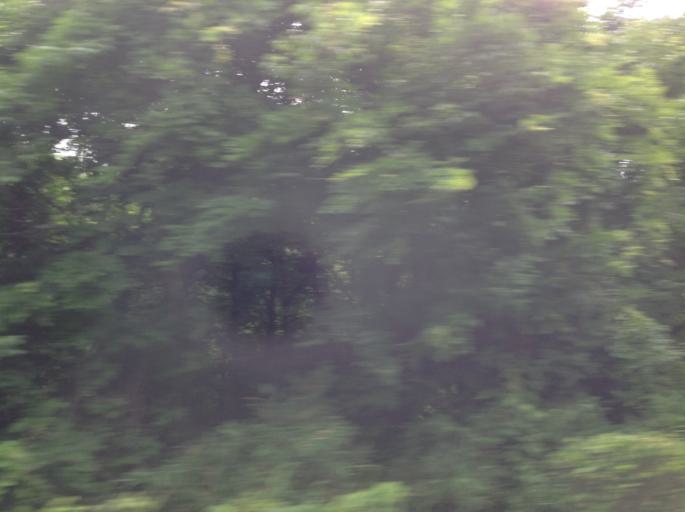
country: JP
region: Miyagi
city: Sendai
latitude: 38.2780
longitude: 140.8099
